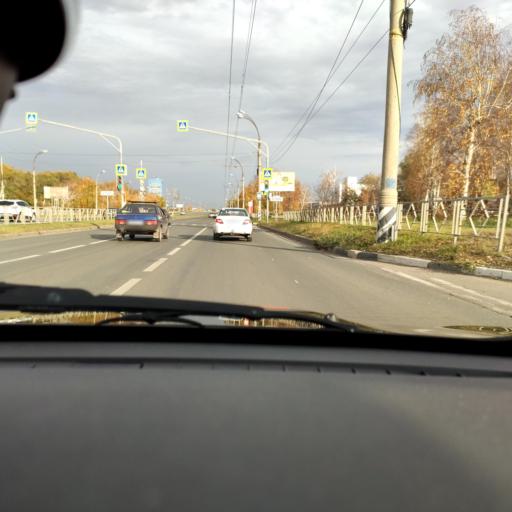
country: RU
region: Samara
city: Tol'yatti
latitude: 53.5416
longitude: 49.2645
